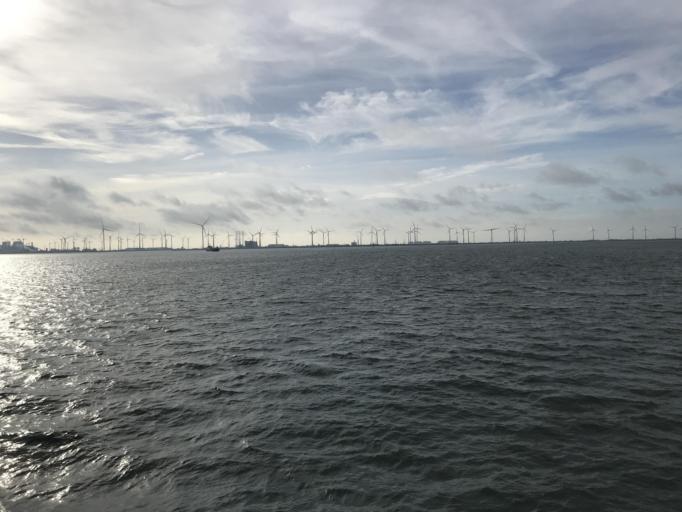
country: DE
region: Lower Saxony
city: Borkum
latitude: 53.4916
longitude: 6.8281
